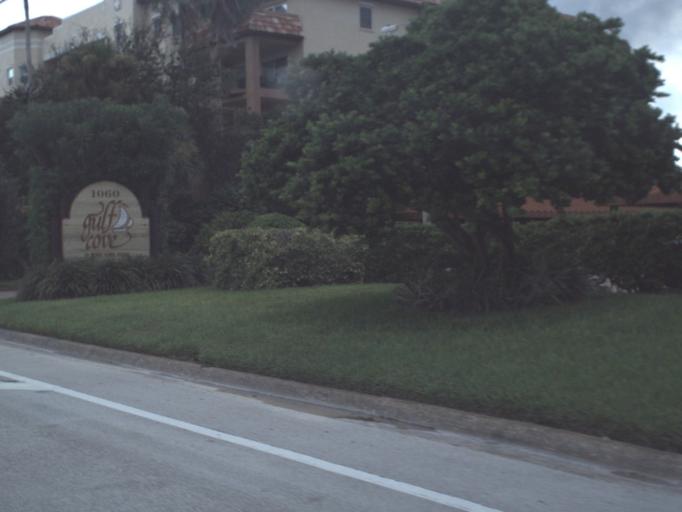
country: US
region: Florida
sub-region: Pinellas County
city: Tierra Verde
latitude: 27.6776
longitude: -82.7260
